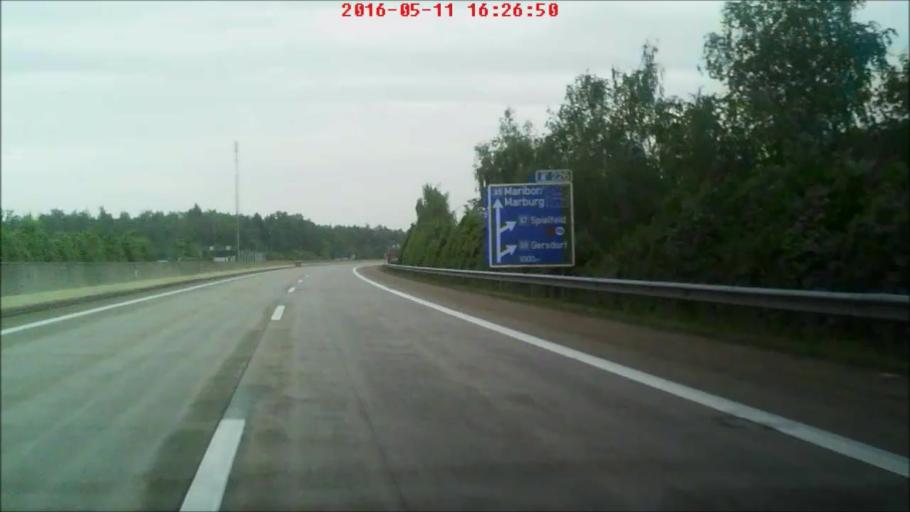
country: AT
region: Styria
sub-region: Politischer Bezirk Leibnitz
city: Strass in Steiermark
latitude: 46.7344
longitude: 15.6384
